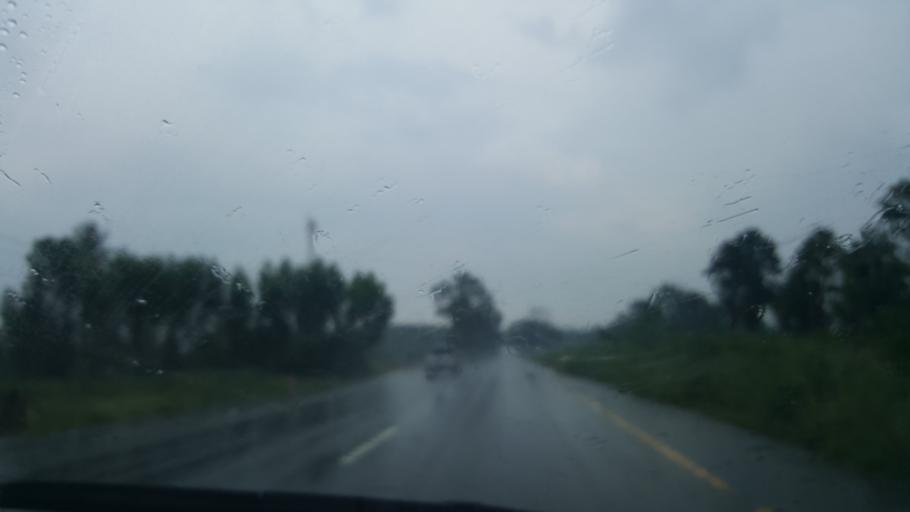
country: TH
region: Chon Buri
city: Phatthaya
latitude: 12.8899
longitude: 101.0248
